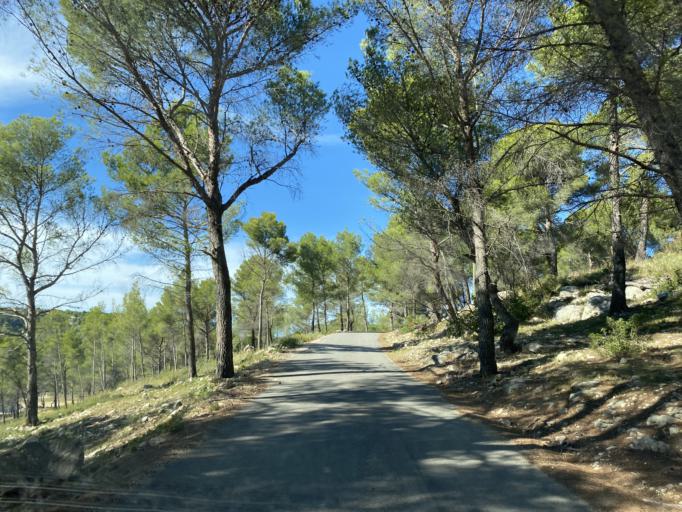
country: FR
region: Provence-Alpes-Cote d'Azur
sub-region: Departement des Bouches-du-Rhone
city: Ceyreste
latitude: 43.2117
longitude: 5.6038
